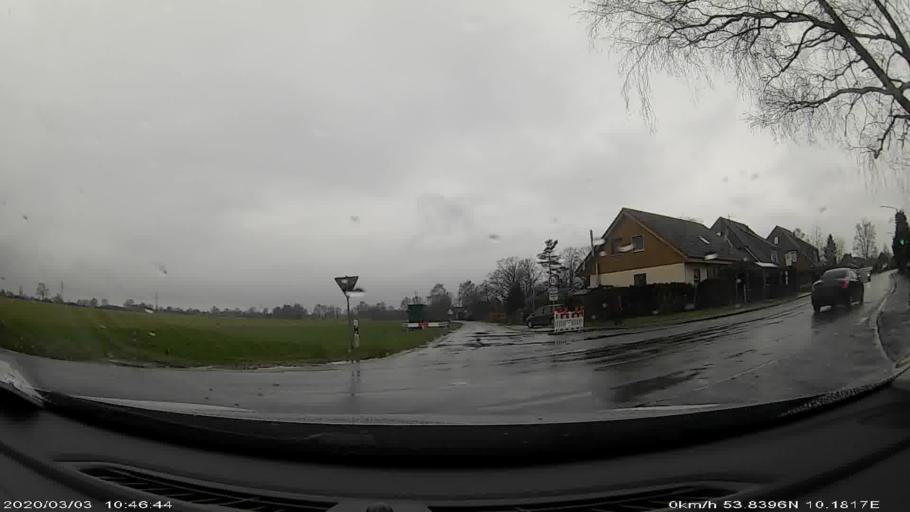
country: DE
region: Schleswig-Holstein
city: Seth
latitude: 53.8388
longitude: 10.1822
